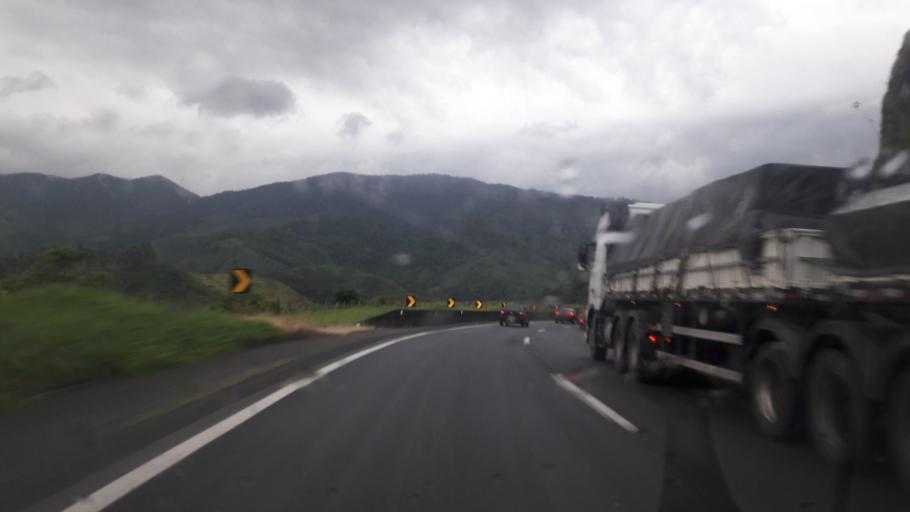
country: BR
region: Sao Paulo
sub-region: Cajati
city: Cajati
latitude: -24.8424
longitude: -48.2121
